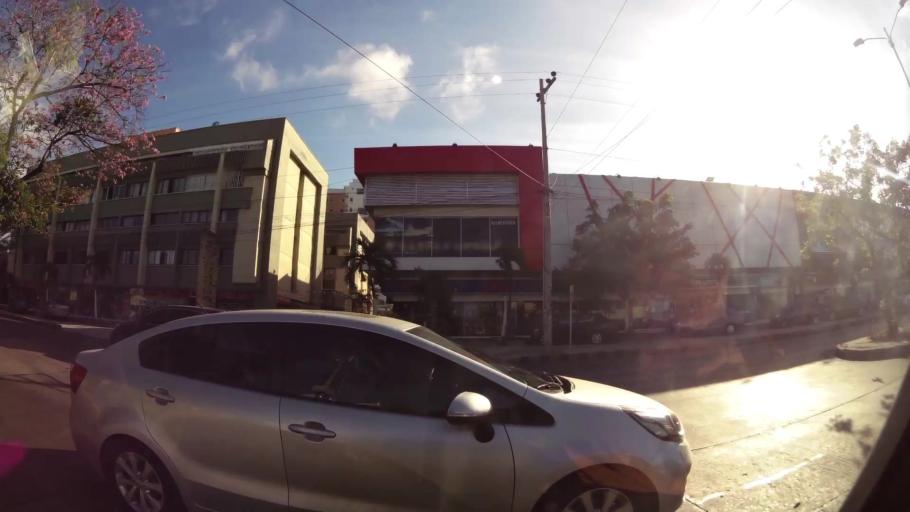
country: CO
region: Atlantico
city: Barranquilla
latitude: 11.0043
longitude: -74.8262
